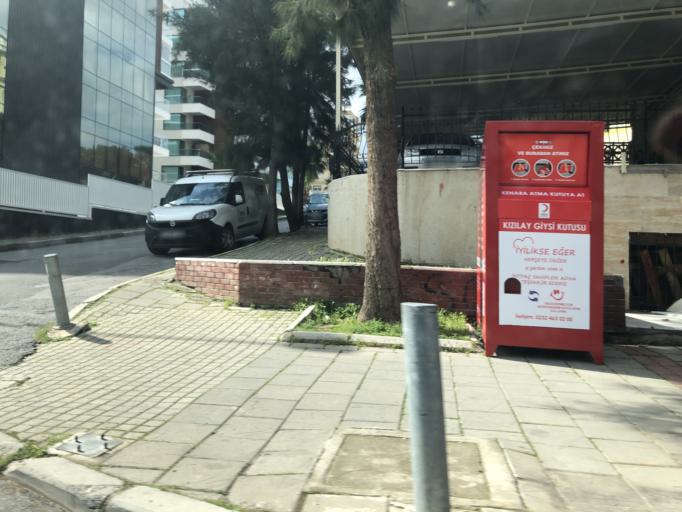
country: TR
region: Izmir
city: Karabaglar
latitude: 38.3907
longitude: 27.0448
